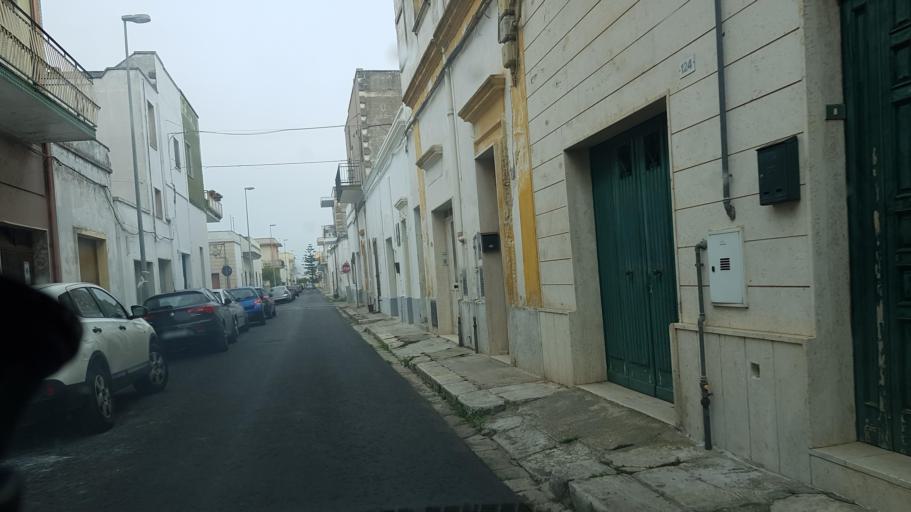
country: IT
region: Apulia
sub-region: Provincia di Lecce
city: Leverano
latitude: 40.2917
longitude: 18.0019
